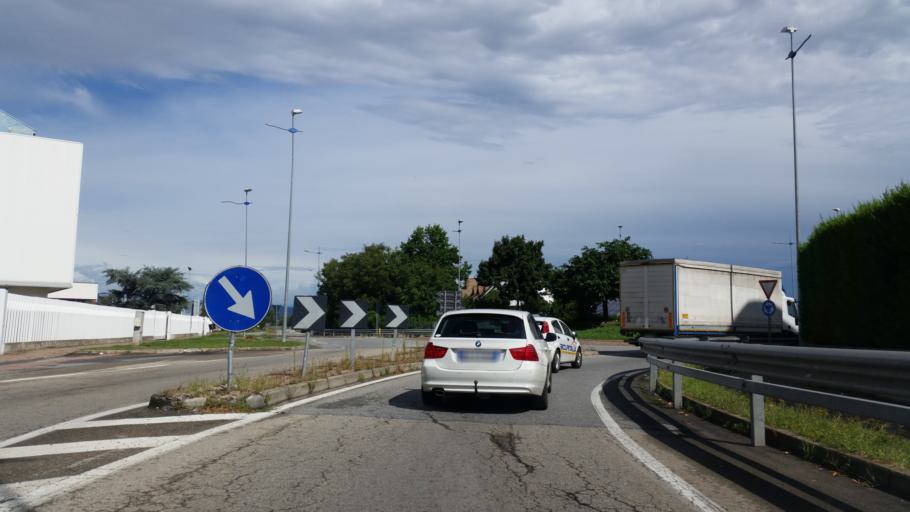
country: IT
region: Piedmont
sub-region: Provincia di Torino
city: Poirino
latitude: 44.9275
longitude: 7.8356
